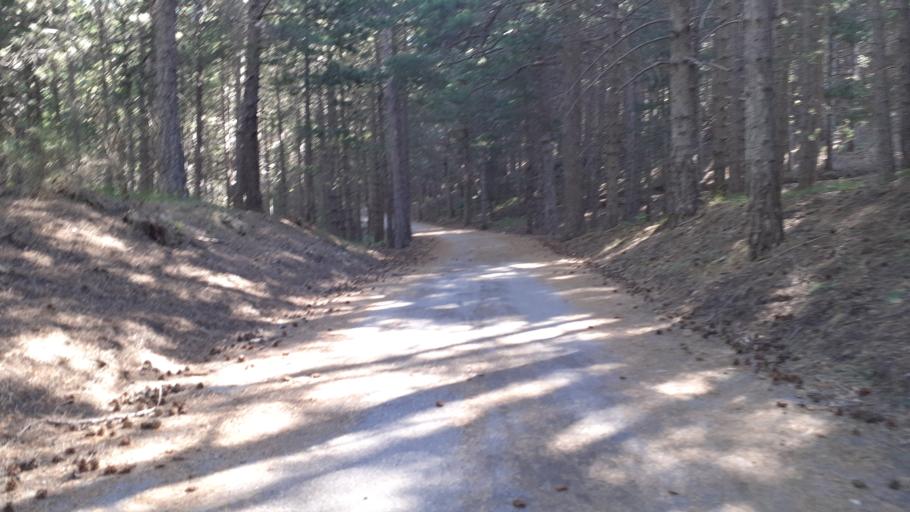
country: IT
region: Sicily
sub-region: Catania
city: Ragalna
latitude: 37.7042
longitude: 14.9609
